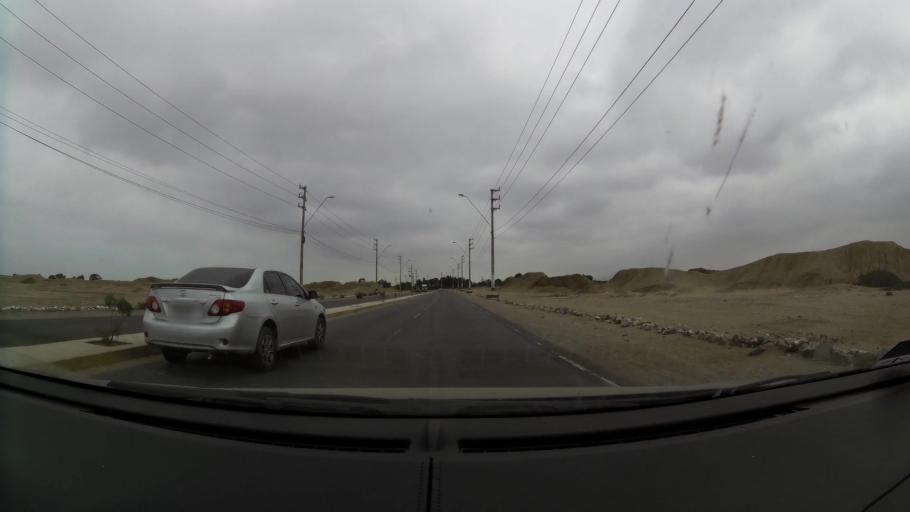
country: PE
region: La Libertad
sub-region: Provincia de Trujillo
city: La Esperanza
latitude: -8.0966
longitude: -79.0700
